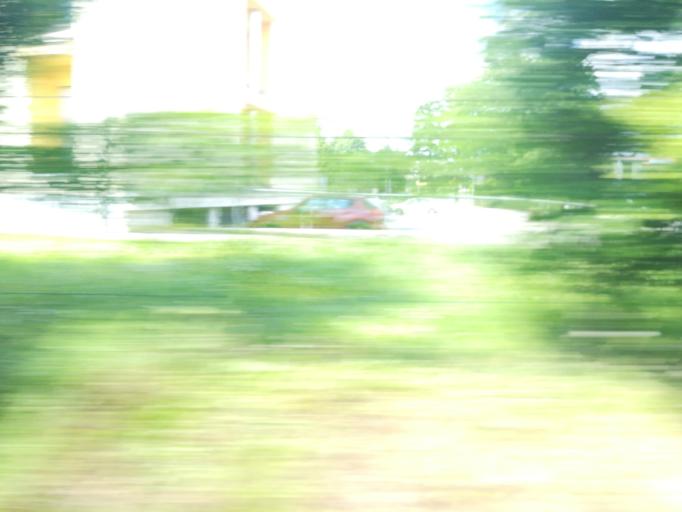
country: IT
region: Veneto
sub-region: Provincia di Vicenza
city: Vicenza
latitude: 45.5432
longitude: 11.5632
